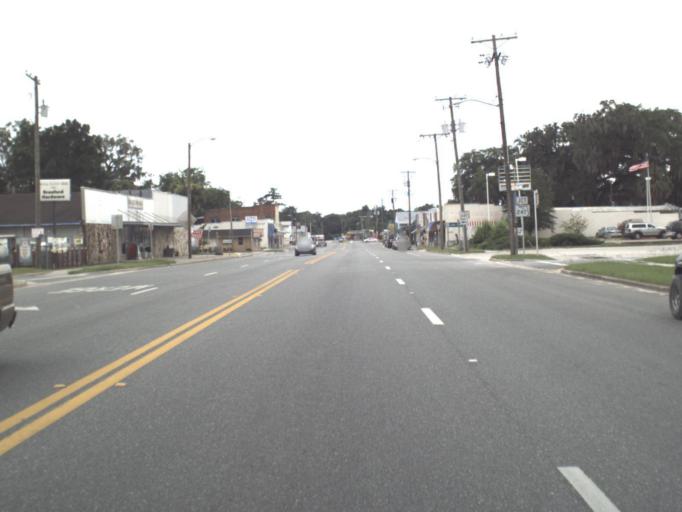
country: US
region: Florida
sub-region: Lafayette County
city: Mayo
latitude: 29.9601
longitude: -82.9297
